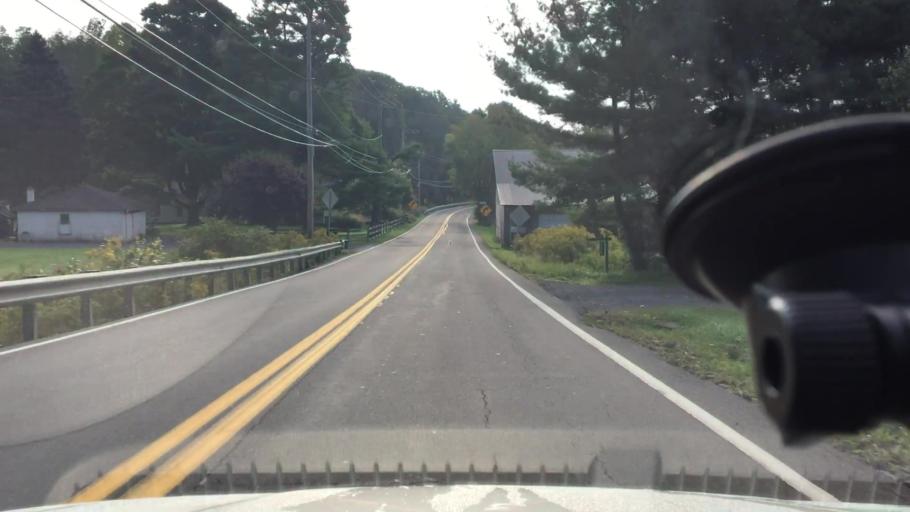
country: US
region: Pennsylvania
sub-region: Monroe County
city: Mount Pocono
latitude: 41.0987
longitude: -75.3361
